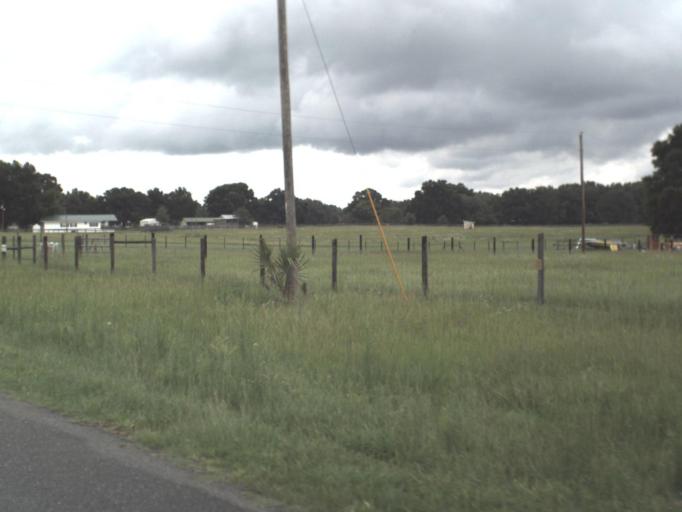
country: US
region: Florida
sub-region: Levy County
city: Williston
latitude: 29.3122
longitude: -82.4510
